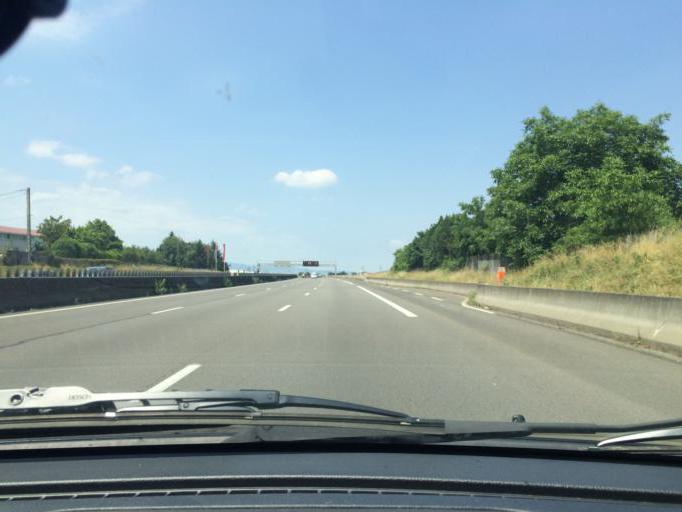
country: FR
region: Rhone-Alpes
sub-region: Departement du Rhone
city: Villefranche-sur-Saone
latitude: 45.9985
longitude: 4.7358
